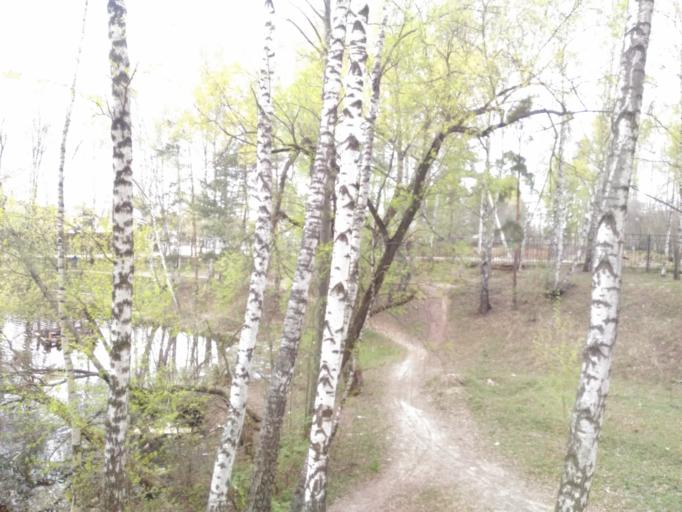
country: RU
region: Moskovskaya
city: Nakhabino
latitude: 55.8462
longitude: 37.1662
